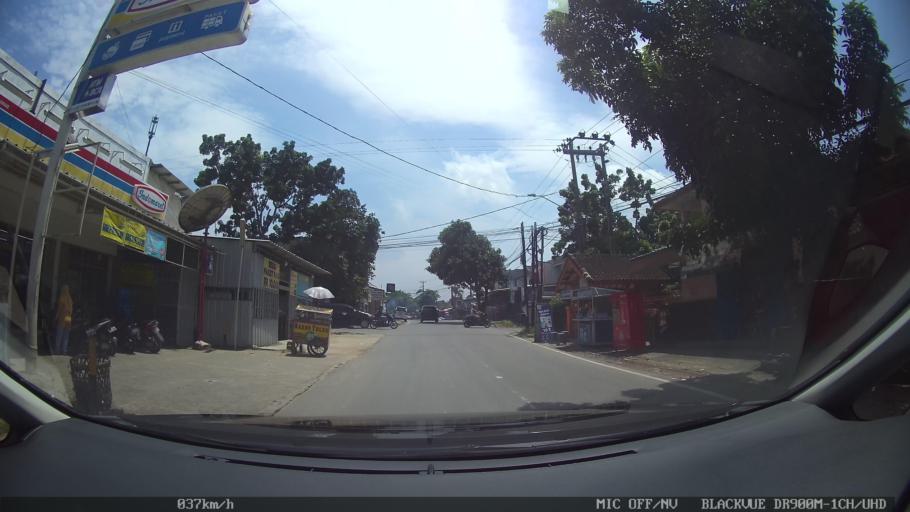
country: ID
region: Lampung
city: Kedaton
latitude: -5.3640
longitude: 105.2894
